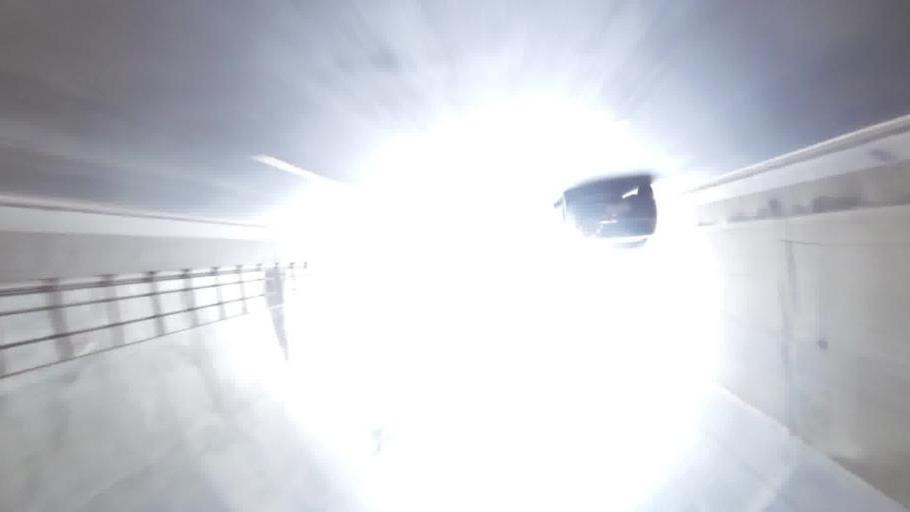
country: BR
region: Rio de Janeiro
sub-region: Rio De Janeiro
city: Rio de Janeiro
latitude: -22.8935
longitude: -43.1936
